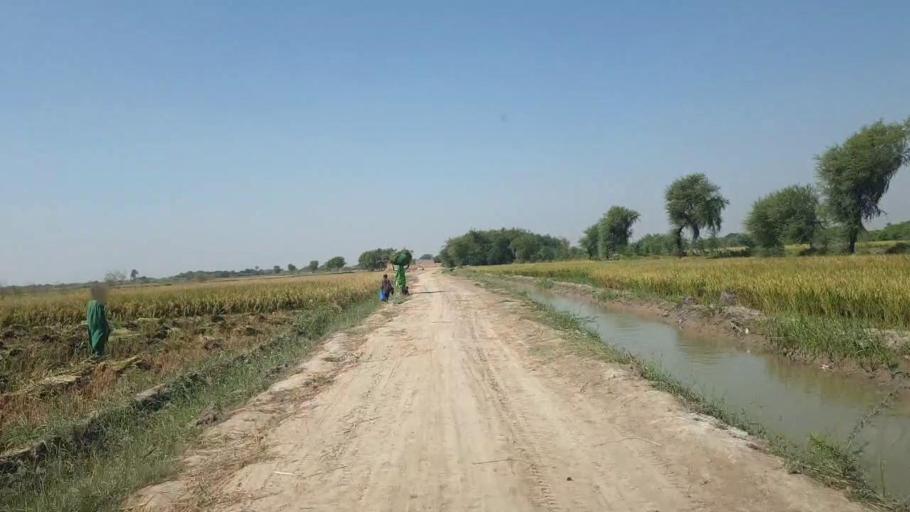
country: PK
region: Sindh
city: Talhar
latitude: 24.8058
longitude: 68.8043
